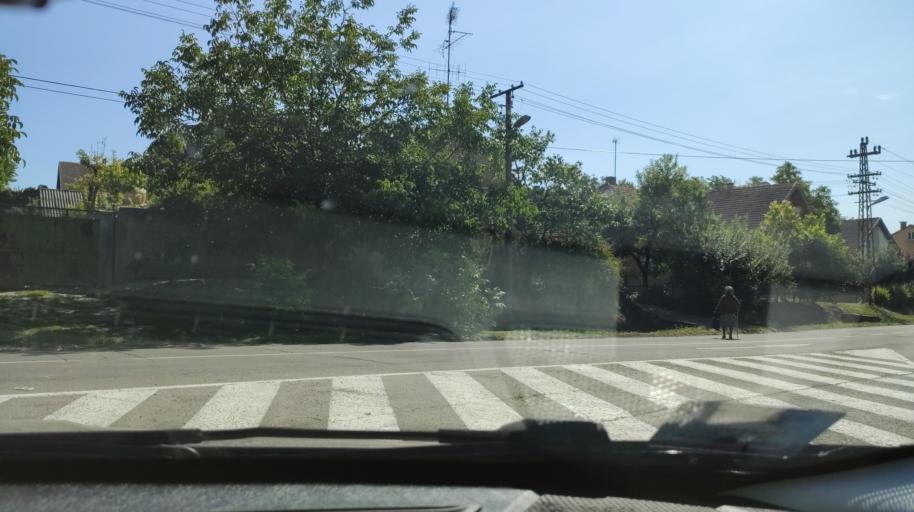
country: RS
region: Autonomna Pokrajina Vojvodina
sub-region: Severnobacki Okrug
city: Backa Topola
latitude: 45.8101
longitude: 19.6365
